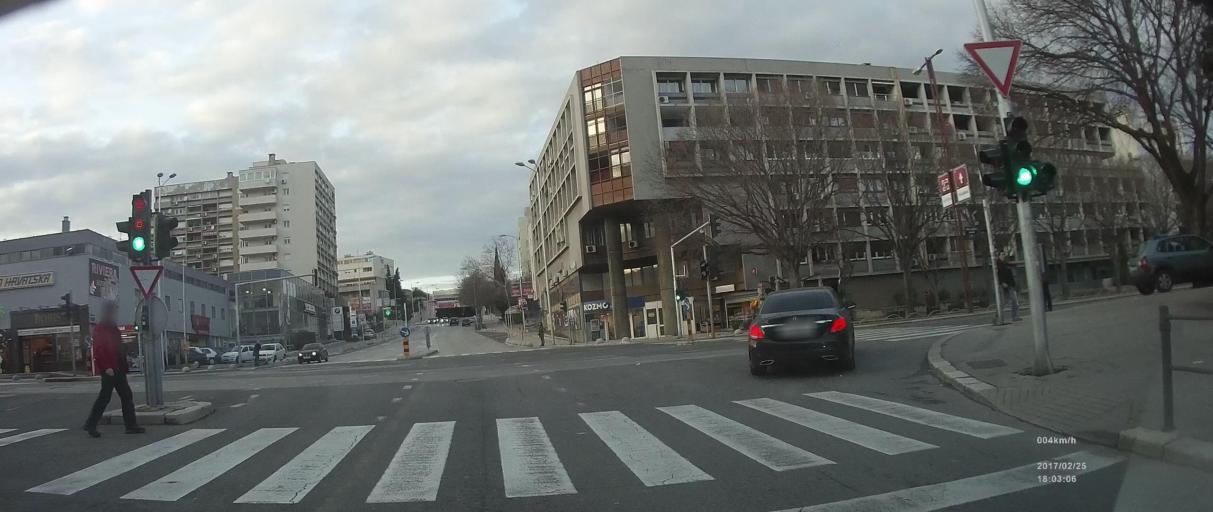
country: HR
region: Splitsko-Dalmatinska
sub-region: Grad Split
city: Split
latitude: 43.5049
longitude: 16.4564
